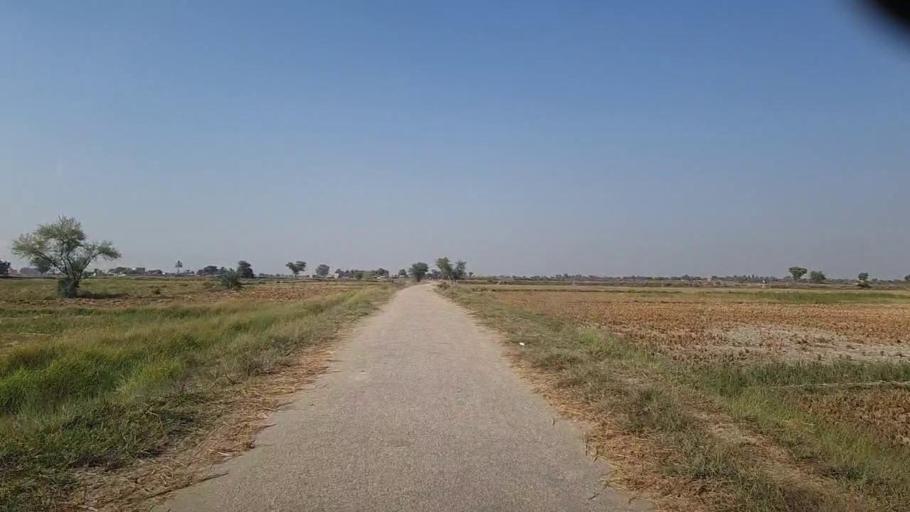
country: PK
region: Sindh
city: Tangwani
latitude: 28.2622
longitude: 68.9339
